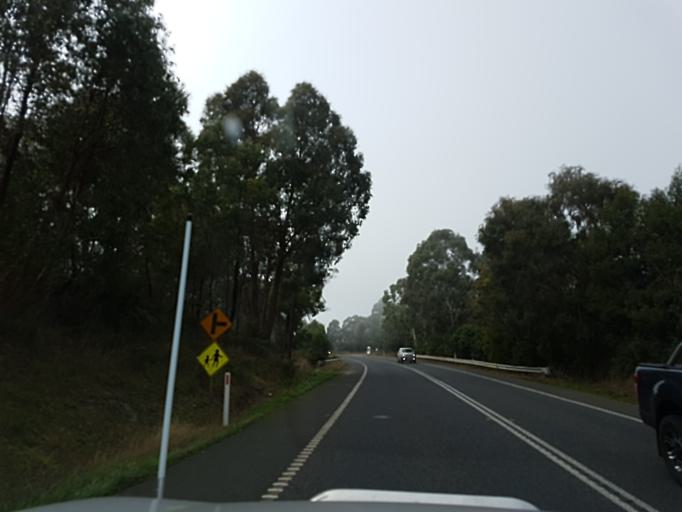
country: AU
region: Victoria
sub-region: Murrindindi
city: Kinglake West
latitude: -37.4147
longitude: 145.4414
